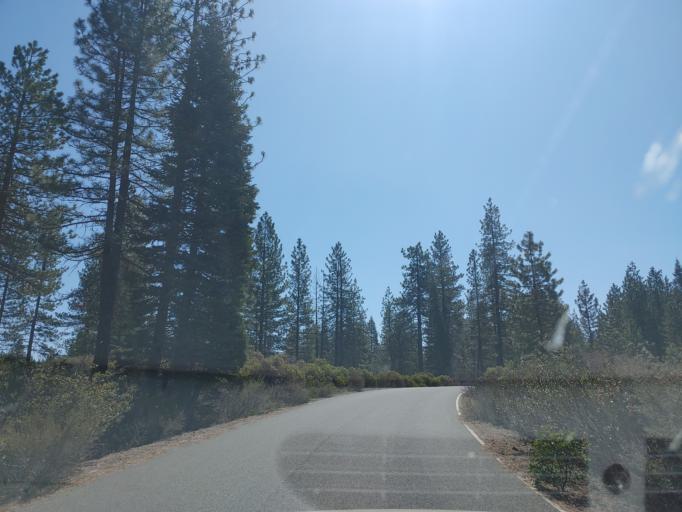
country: US
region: California
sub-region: Siskiyou County
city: McCloud
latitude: 41.2445
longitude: -122.0080
